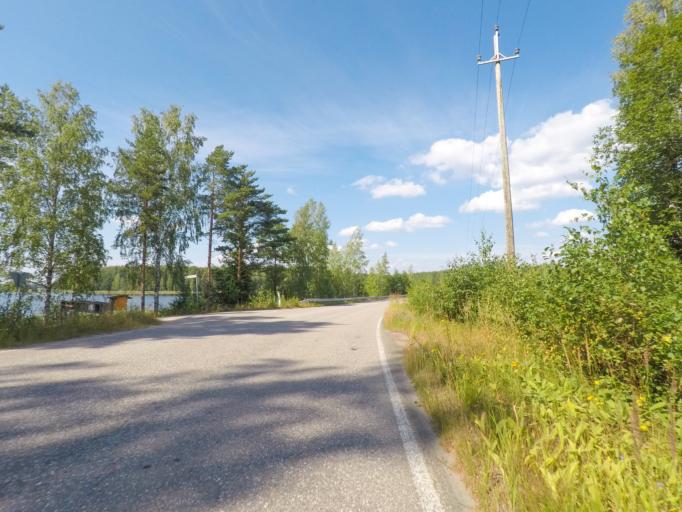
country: FI
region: Southern Savonia
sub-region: Mikkeli
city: Puumala
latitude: 61.4709
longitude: 28.1669
